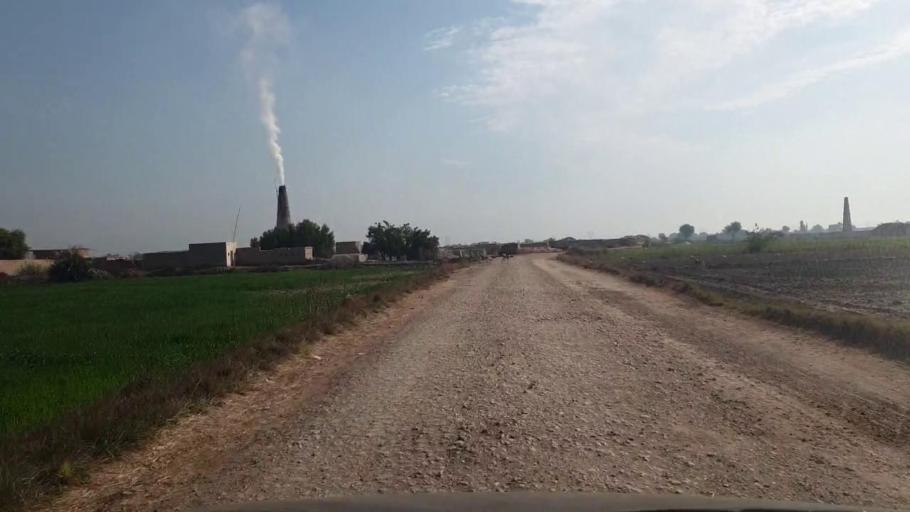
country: PK
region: Sindh
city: Hala
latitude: 25.9885
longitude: 68.3882
